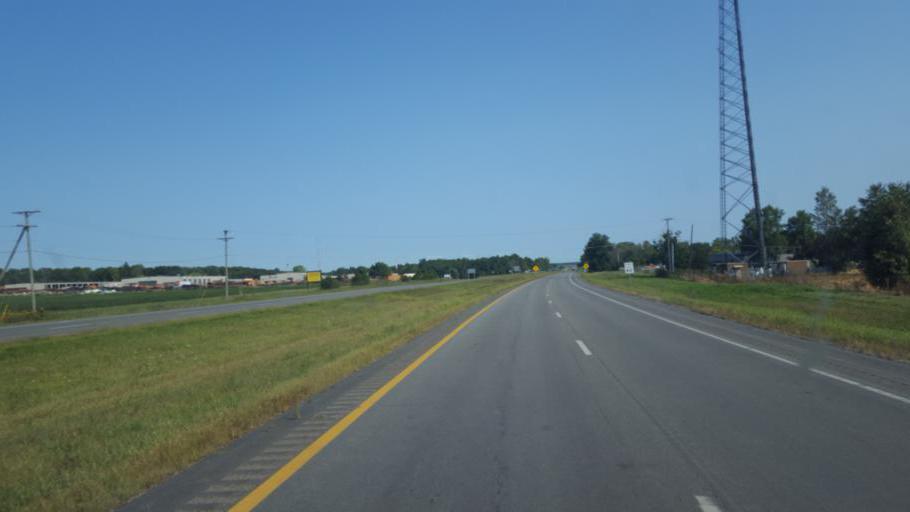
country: US
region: Ohio
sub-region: Knox County
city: Fredericktown
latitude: 40.4859
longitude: -82.5591
